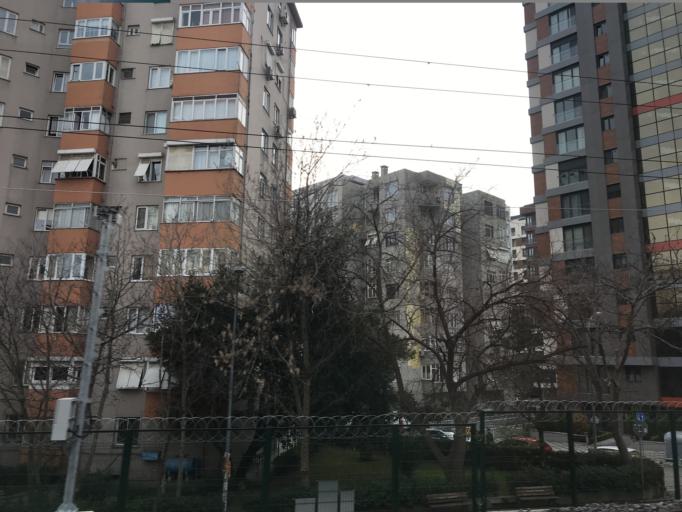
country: TR
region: Istanbul
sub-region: Atasehir
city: Atasehir
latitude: 40.9682
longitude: 29.0780
